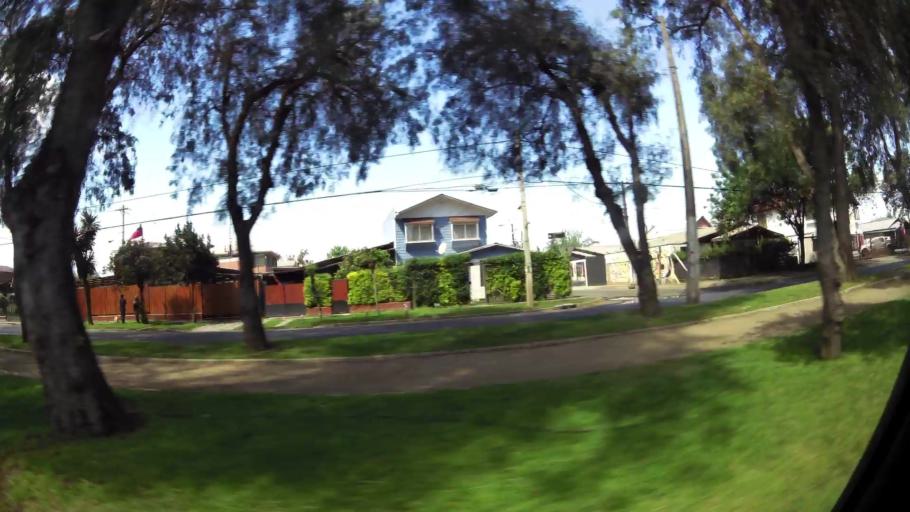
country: CL
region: Santiago Metropolitan
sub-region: Provincia de Santiago
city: Lo Prado
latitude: -33.4777
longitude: -70.7286
